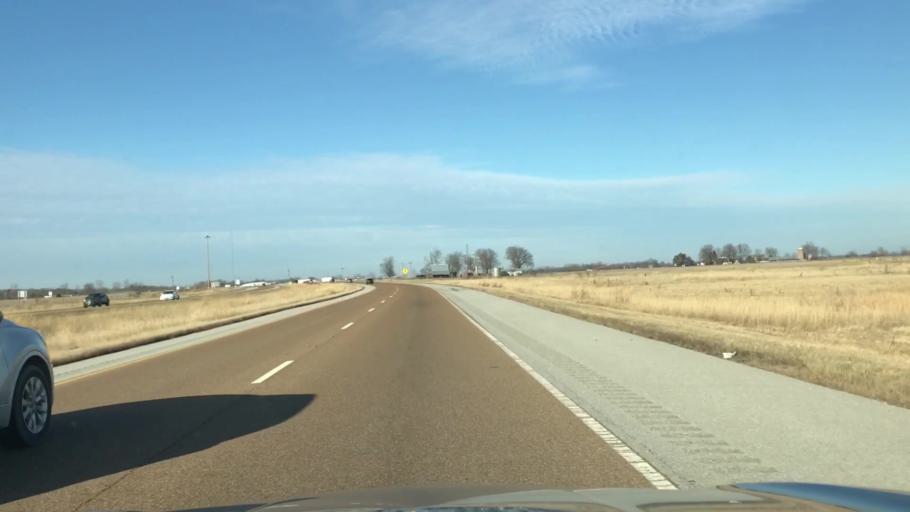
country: US
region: Illinois
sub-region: Macoupin County
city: Staunton
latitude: 39.0216
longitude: -89.7495
